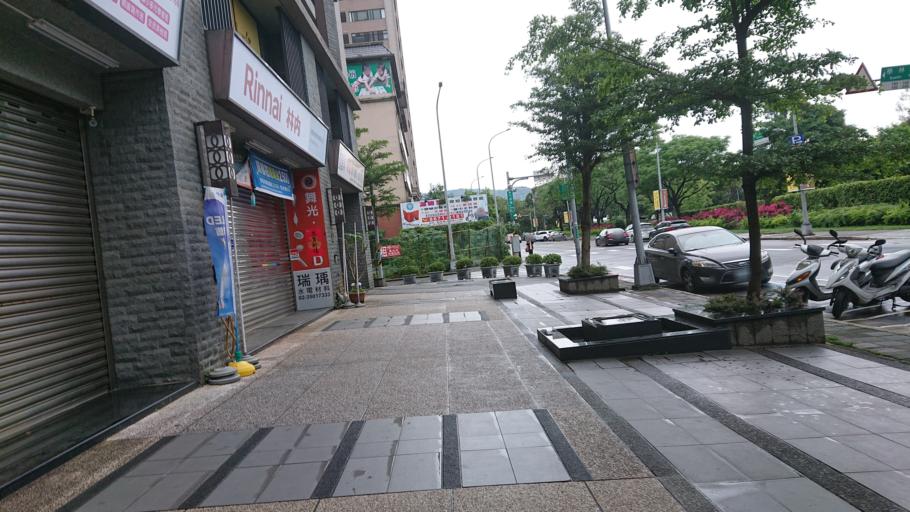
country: TW
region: Taiwan
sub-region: Taoyuan
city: Taoyuan
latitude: 24.9495
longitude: 121.3814
